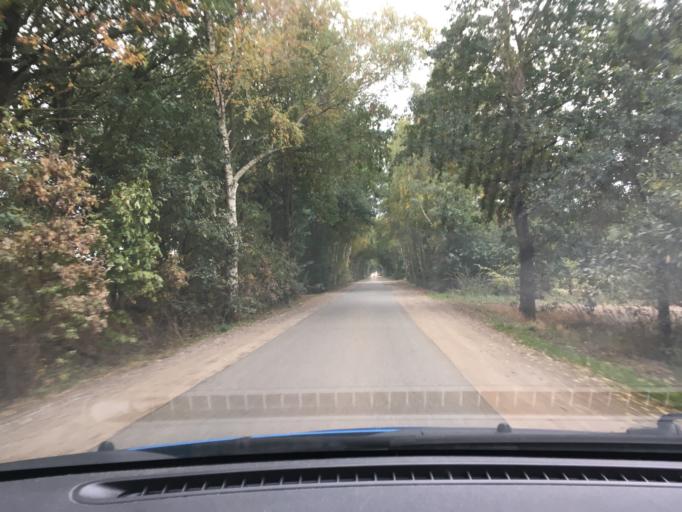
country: DE
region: Lower Saxony
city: Winsen
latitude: 53.3675
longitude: 10.2378
